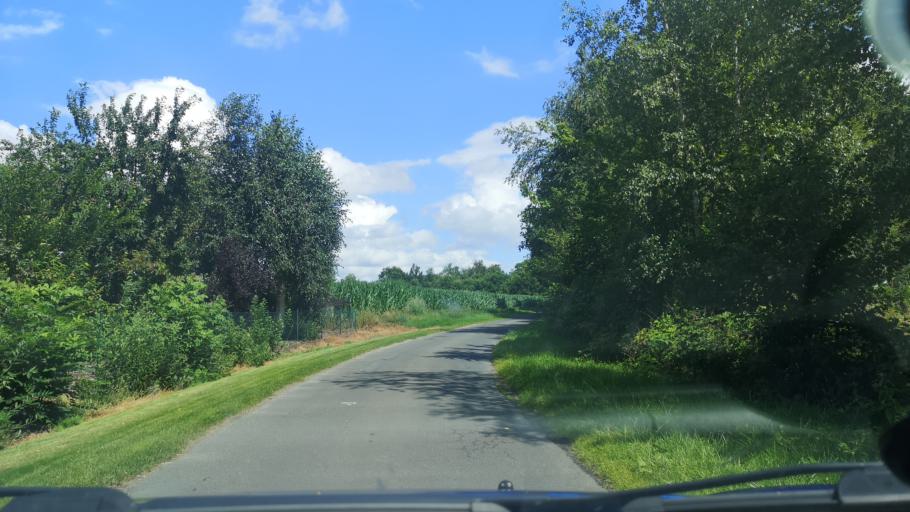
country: DE
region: Lower Saxony
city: Langen
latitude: 53.6399
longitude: 8.6124
